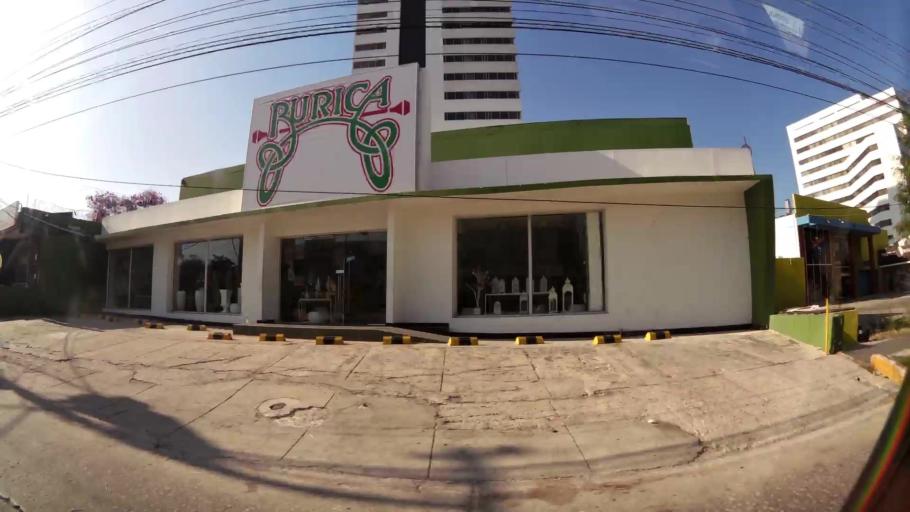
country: CO
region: Atlantico
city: Barranquilla
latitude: 11.0083
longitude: -74.8016
